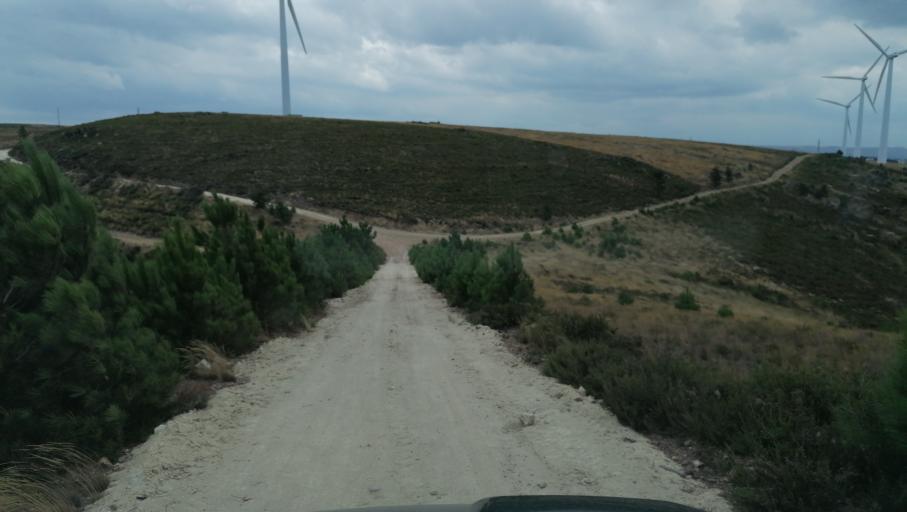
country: PT
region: Vila Real
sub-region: Ribeira de Pena
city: Sobreira
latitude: 41.5327
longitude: -7.7235
